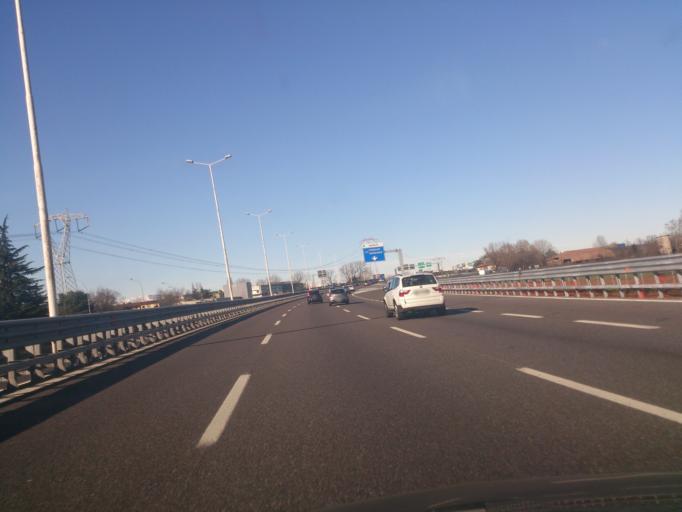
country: IT
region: Lombardy
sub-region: Citta metropolitana di Milano
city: Trezzano sul Naviglio
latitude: 45.4178
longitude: 9.0845
